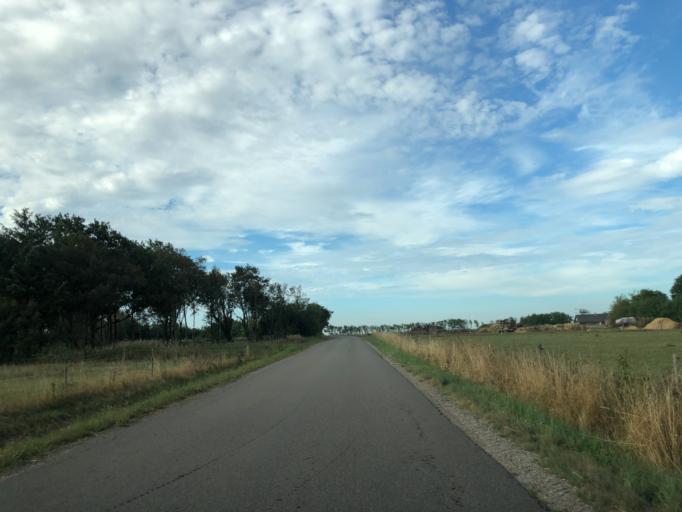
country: DK
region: Central Jutland
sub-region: Holstebro Kommune
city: Ulfborg
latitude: 56.1570
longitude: 8.4088
